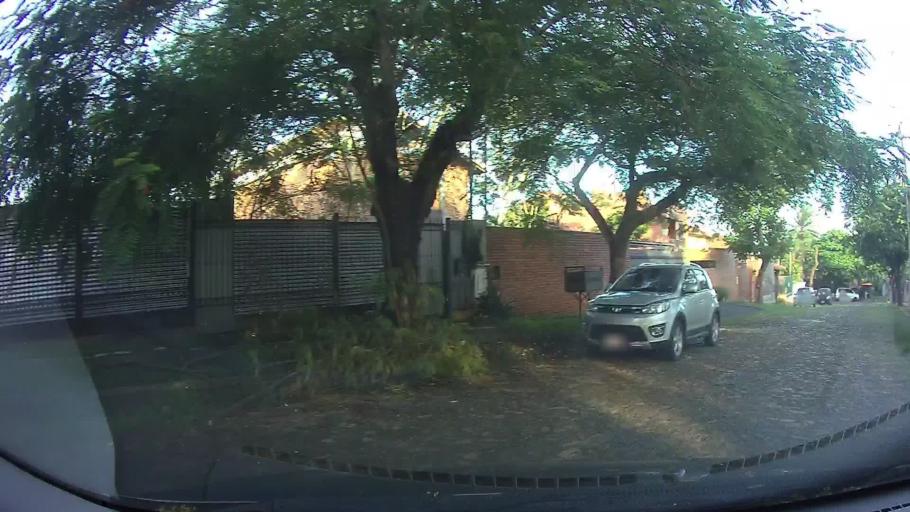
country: PY
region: Asuncion
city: Asuncion
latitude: -25.2699
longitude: -57.5666
